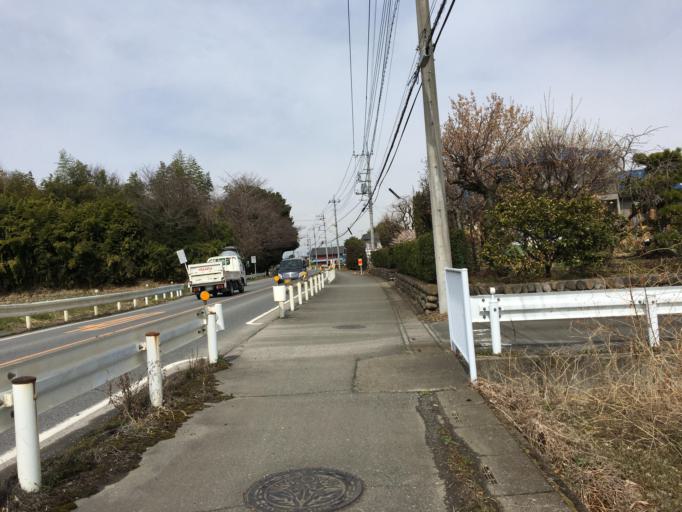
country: JP
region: Saitama
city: Yorii
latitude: 36.1443
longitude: 139.2087
